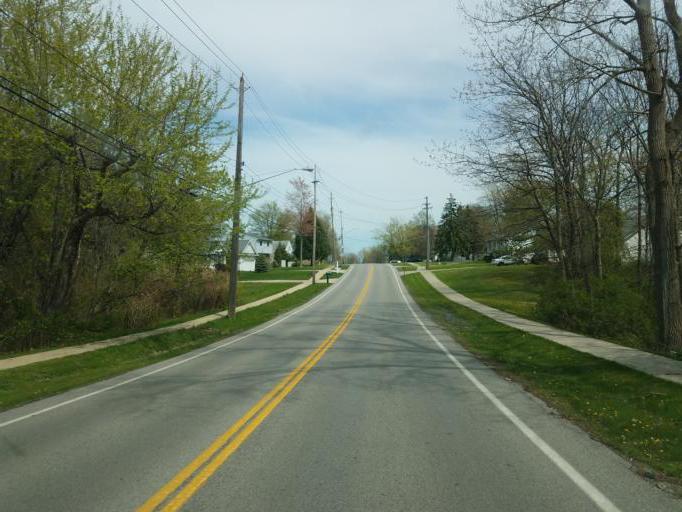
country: US
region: Ohio
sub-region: Lake County
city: Mentor-on-the-Lake
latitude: 41.7203
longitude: -81.3571
